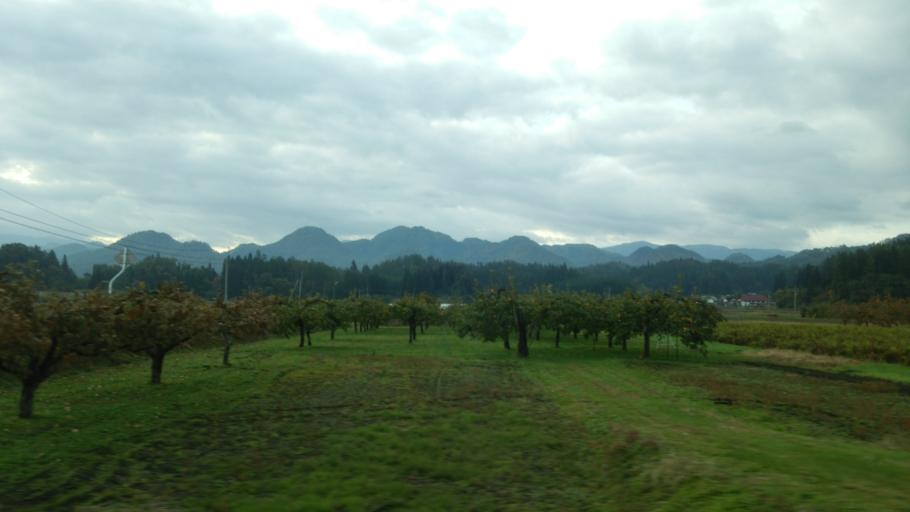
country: JP
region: Fukushima
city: Kitakata
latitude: 37.4352
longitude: 139.8281
